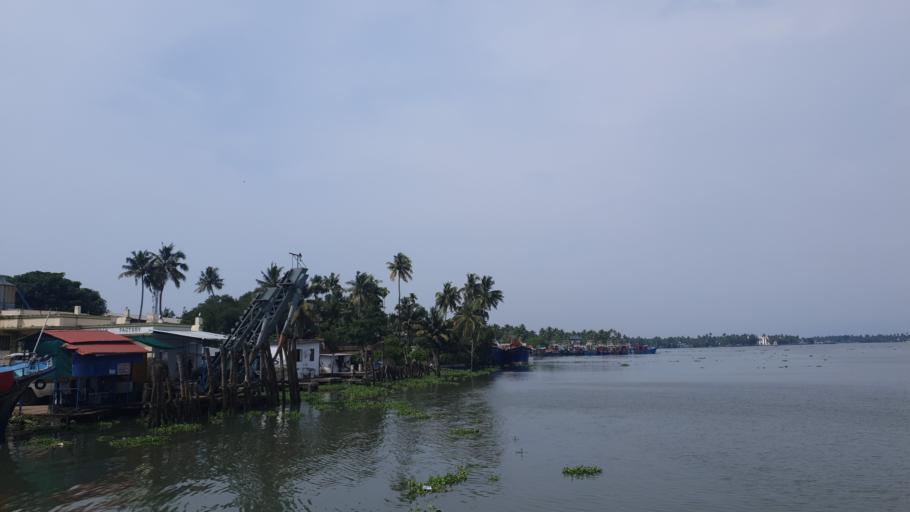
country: IN
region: Kerala
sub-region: Ernakulam
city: Cochin
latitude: 9.9885
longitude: 76.2404
